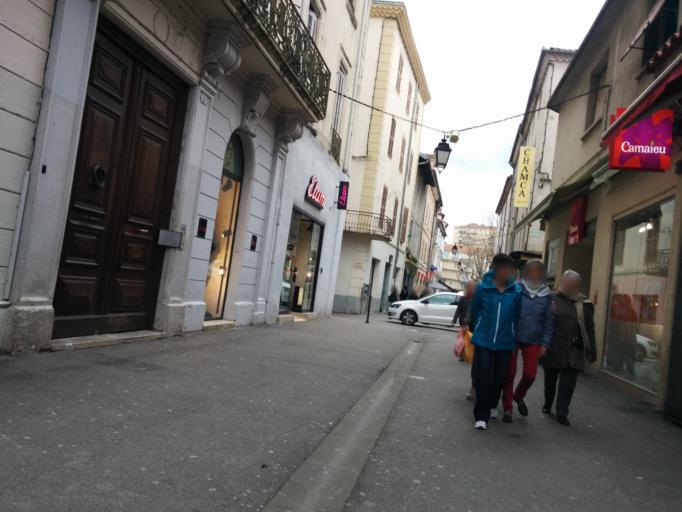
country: FR
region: Languedoc-Roussillon
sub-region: Departement du Gard
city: Ales
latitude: 44.1225
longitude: 4.0798
